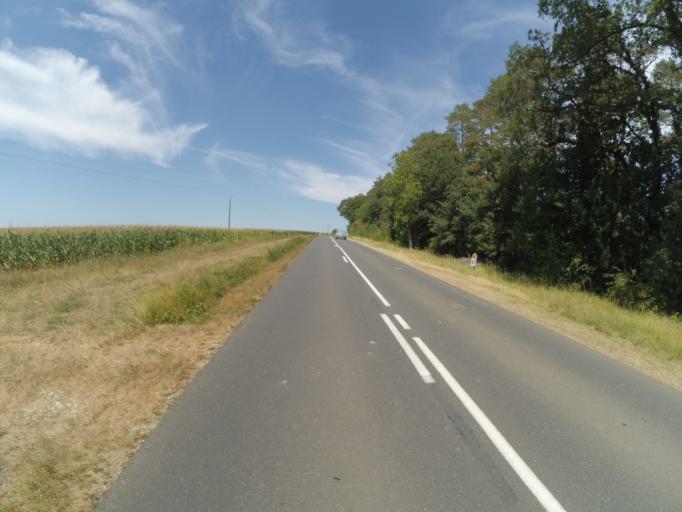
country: FR
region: Poitou-Charentes
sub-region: Departement de la Vienne
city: Usson-du-Poitou
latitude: 46.2495
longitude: 0.5235
